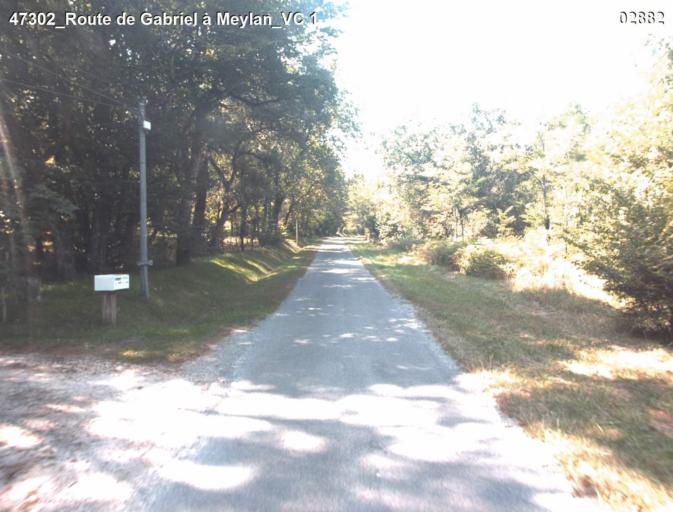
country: FR
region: Aquitaine
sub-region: Departement du Lot-et-Garonne
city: Mezin
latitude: 44.0722
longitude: 0.1286
